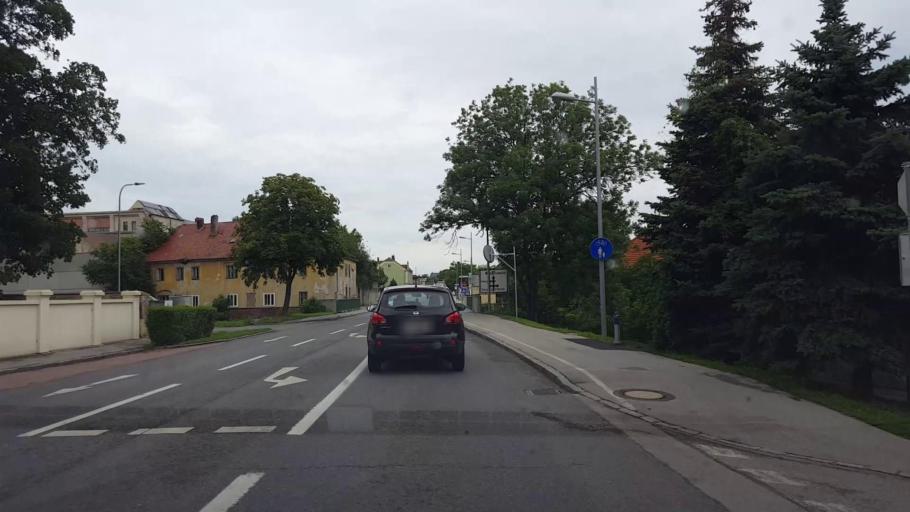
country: AT
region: Lower Austria
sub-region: Politischer Bezirk Wien-Umgebung
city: Schwadorf
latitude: 48.0699
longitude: 16.5855
